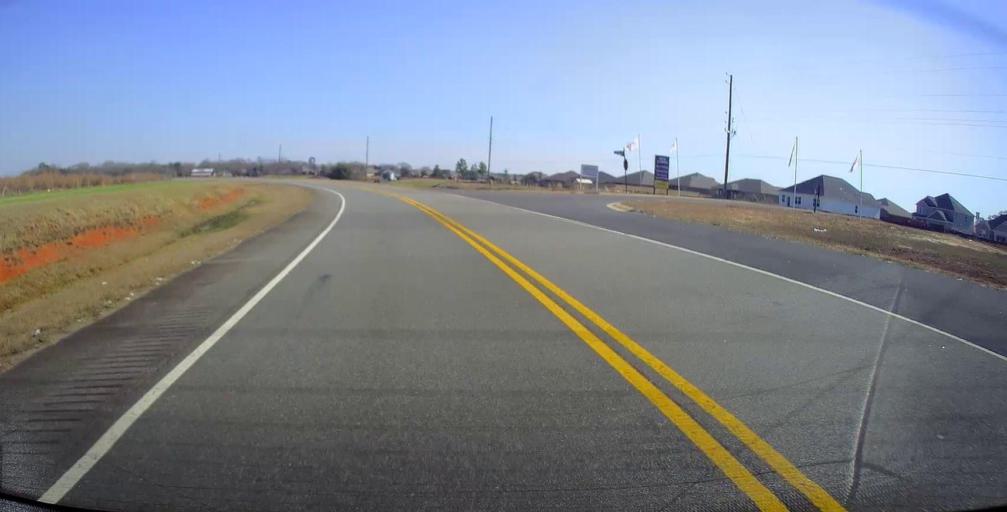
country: US
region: Georgia
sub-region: Houston County
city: Perry
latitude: 32.4369
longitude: -83.7780
